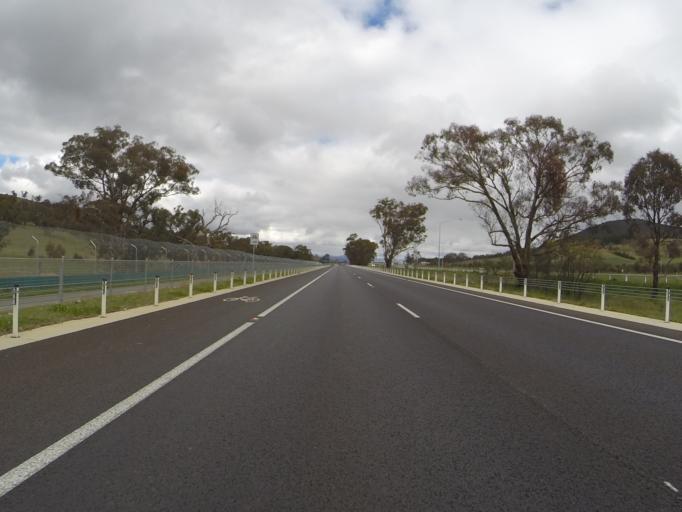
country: AU
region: Australian Capital Territory
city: Canberra
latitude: -35.2229
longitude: 149.1962
